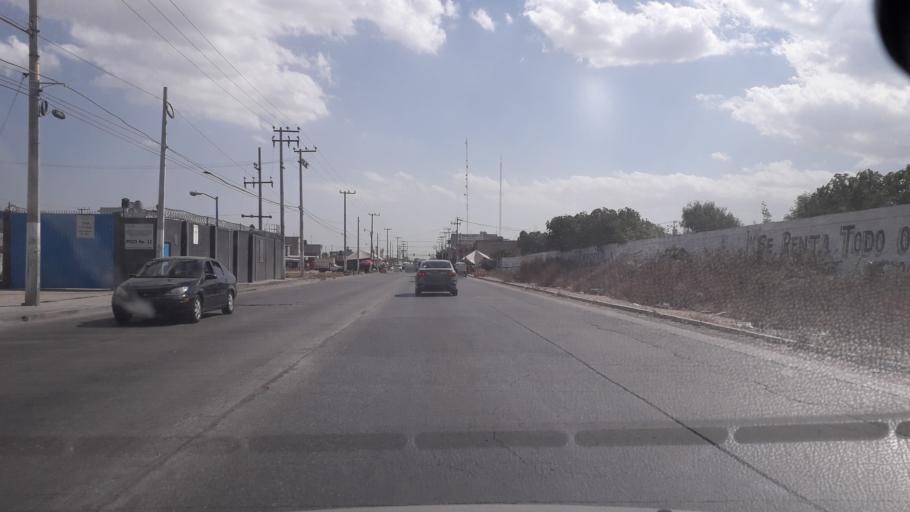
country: MX
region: Mexico
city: Ecatepec
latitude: 19.6269
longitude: -99.0499
